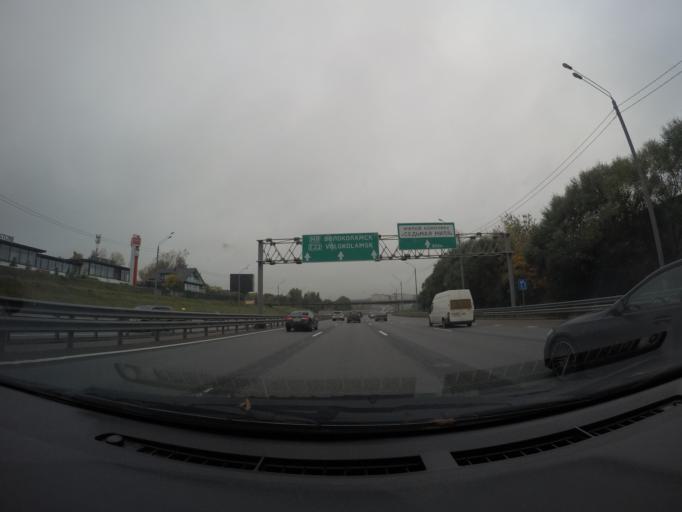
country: RU
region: Moskovskaya
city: Petrovo-Dal'neye
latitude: 55.7747
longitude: 37.2034
